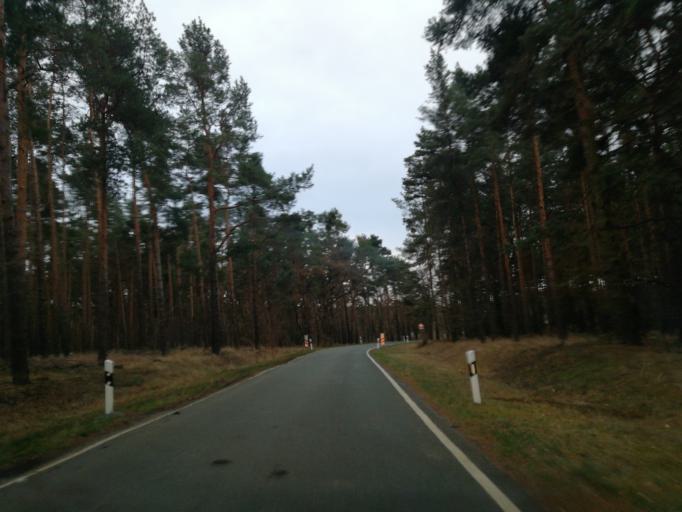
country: DE
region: Brandenburg
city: Vetschau
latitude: 51.7464
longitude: 14.1327
